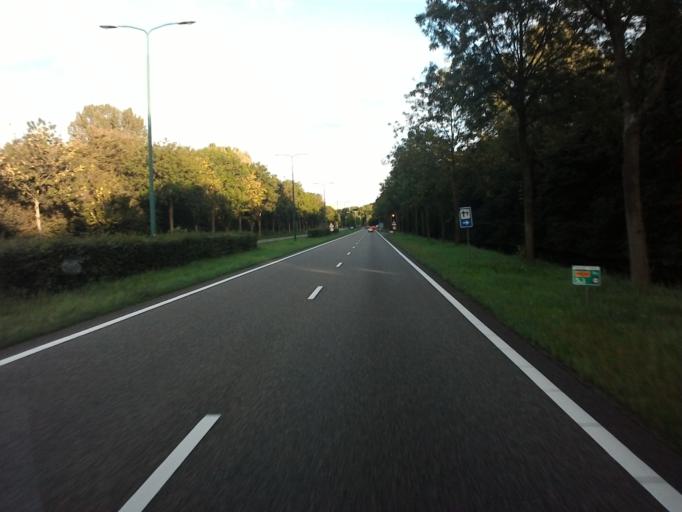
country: NL
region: Utrecht
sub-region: Gemeente Utrecht
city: Utrecht
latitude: 52.1313
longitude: 5.0930
